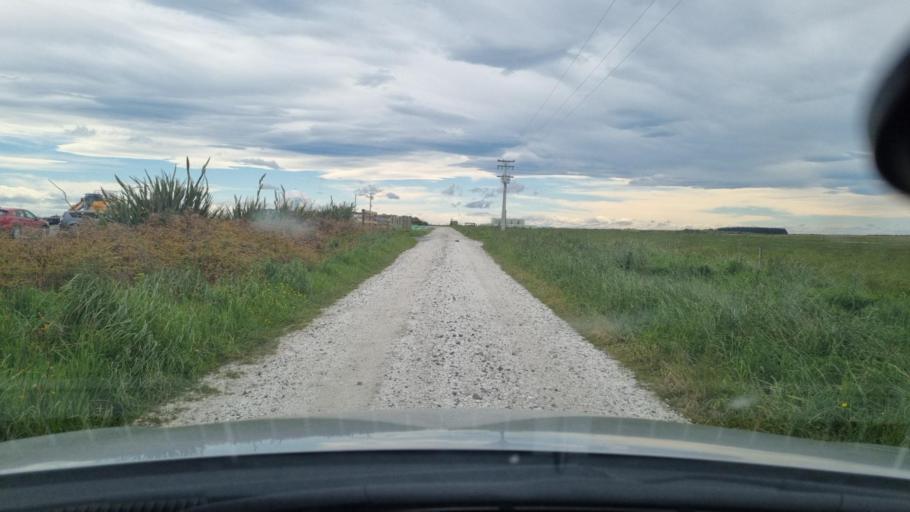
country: NZ
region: Southland
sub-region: Invercargill City
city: Bluff
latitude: -46.5301
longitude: 168.3830
